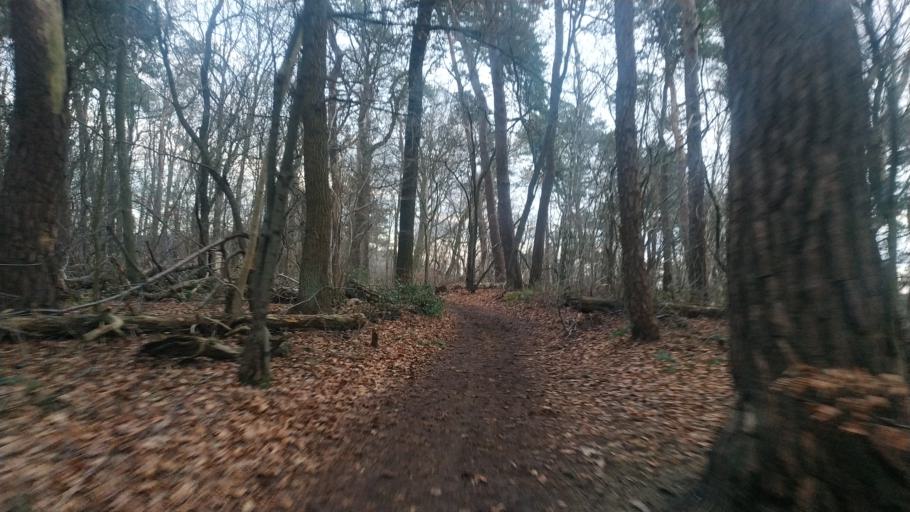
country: DE
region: North Rhine-Westphalia
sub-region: Regierungsbezirk Munster
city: Horstel
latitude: 52.2799
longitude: 7.6020
